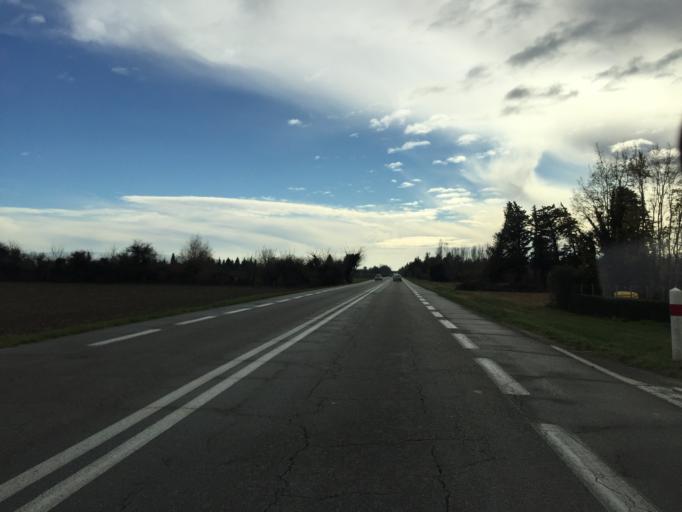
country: FR
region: Provence-Alpes-Cote d'Azur
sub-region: Departement du Vaucluse
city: Velleron
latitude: 43.9469
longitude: 5.0277
